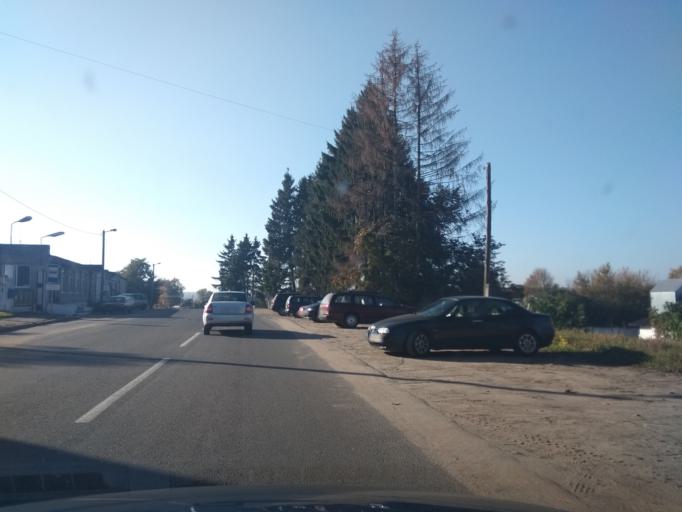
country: BY
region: Grodnenskaya
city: Vawkavysk
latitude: 53.1564
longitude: 24.4602
